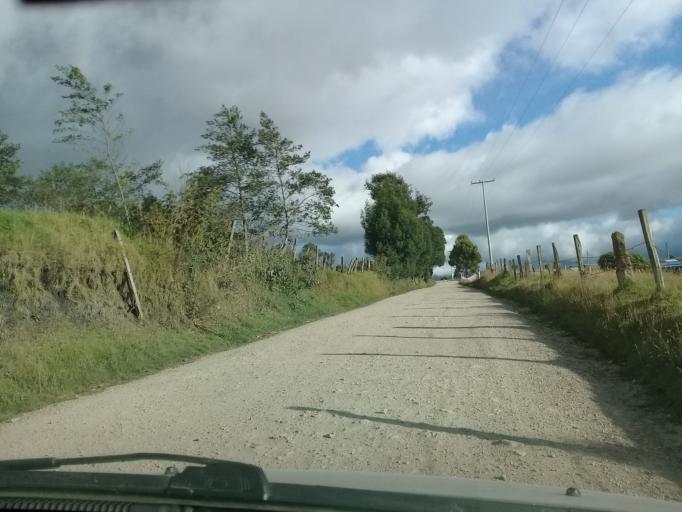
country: CO
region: Cundinamarca
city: Villapinzon
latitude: 5.2401
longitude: -73.6532
